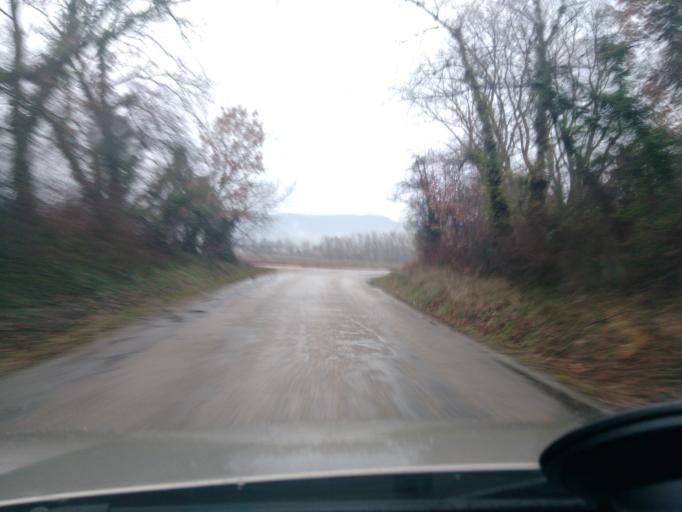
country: FR
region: Rhone-Alpes
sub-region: Departement de l'Ardeche
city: Le Teil
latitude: 44.5494
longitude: 4.7137
